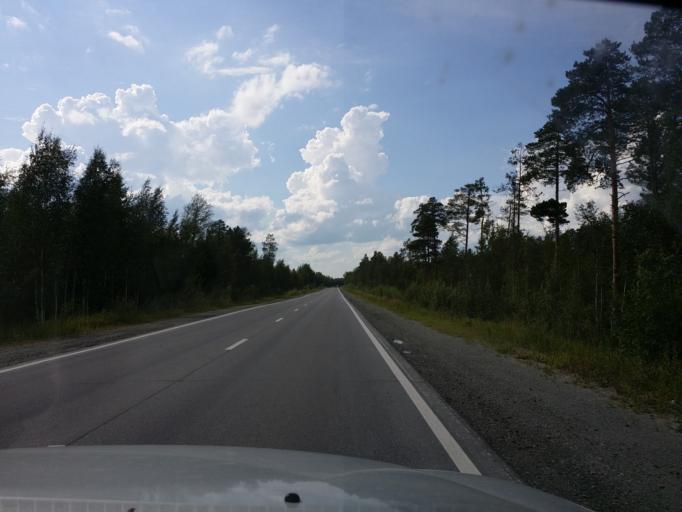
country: RU
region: Khanty-Mansiyskiy Avtonomnyy Okrug
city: Megion
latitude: 61.1270
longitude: 75.8064
